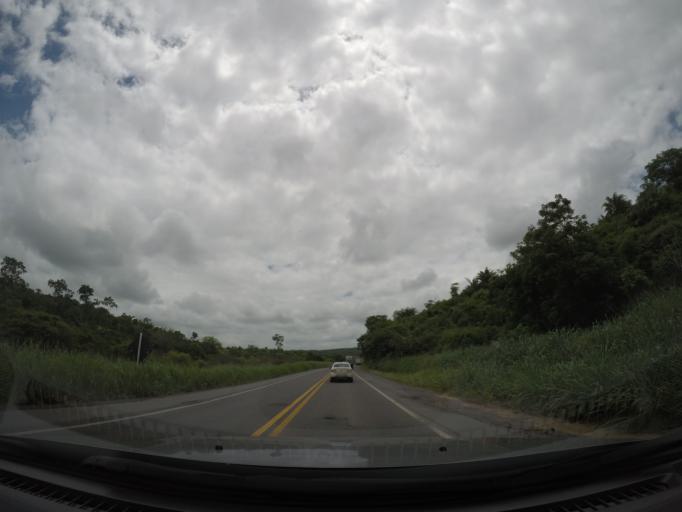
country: BR
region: Bahia
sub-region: Ruy Barbosa
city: Terra Nova
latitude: -12.4616
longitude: -40.5657
